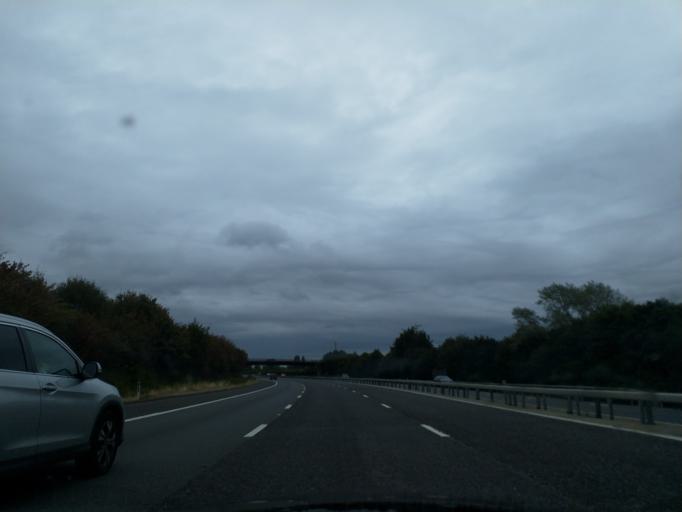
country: GB
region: England
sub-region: Surrey
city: Shepperton
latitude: 51.3962
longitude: -0.4563
